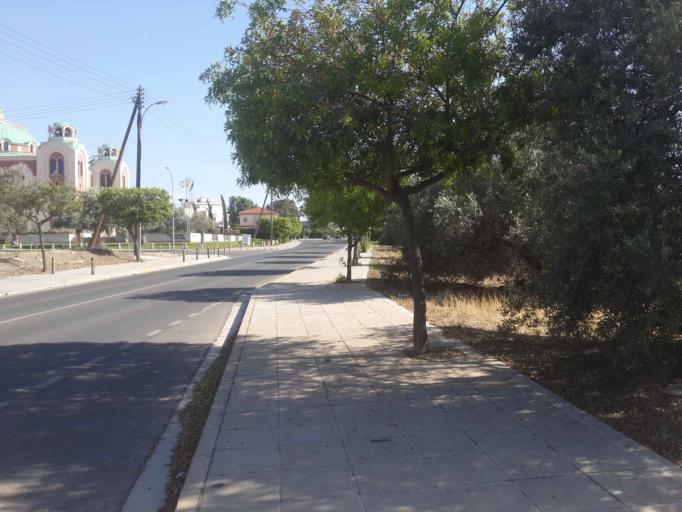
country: CY
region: Lefkosia
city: Nicosia
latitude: 35.1488
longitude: 33.3343
